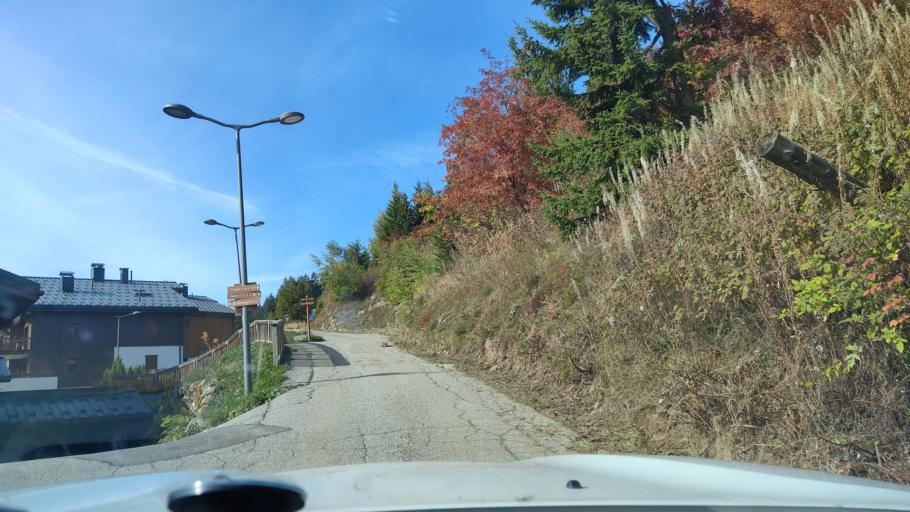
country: FR
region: Rhone-Alpes
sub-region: Departement de la Savoie
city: Beaufort
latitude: 45.7372
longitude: 6.5000
